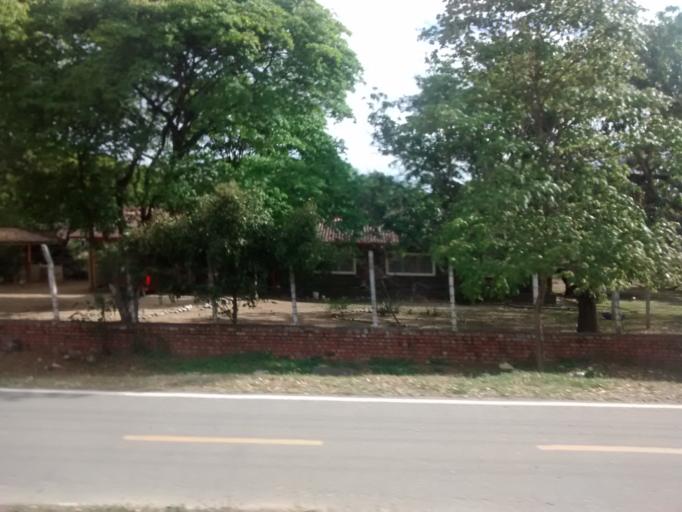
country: CO
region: Cundinamarca
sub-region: Girardot
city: Girardot City
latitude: 4.2950
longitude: -74.7863
